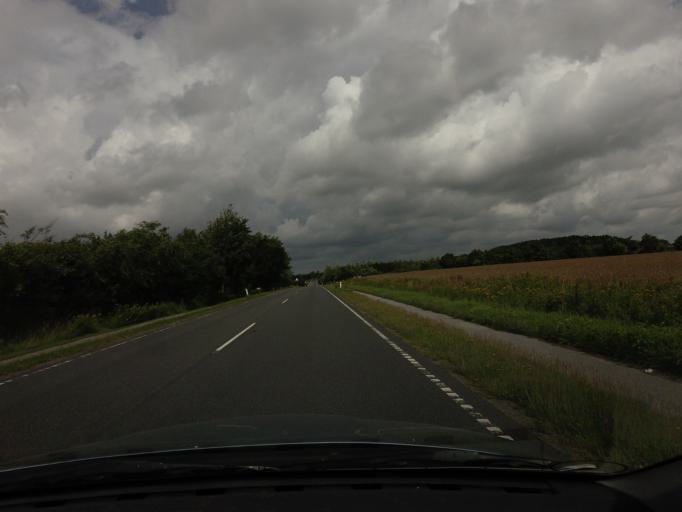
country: DK
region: North Denmark
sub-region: Hjorring Kommune
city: Tars
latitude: 57.4041
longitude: 10.0762
